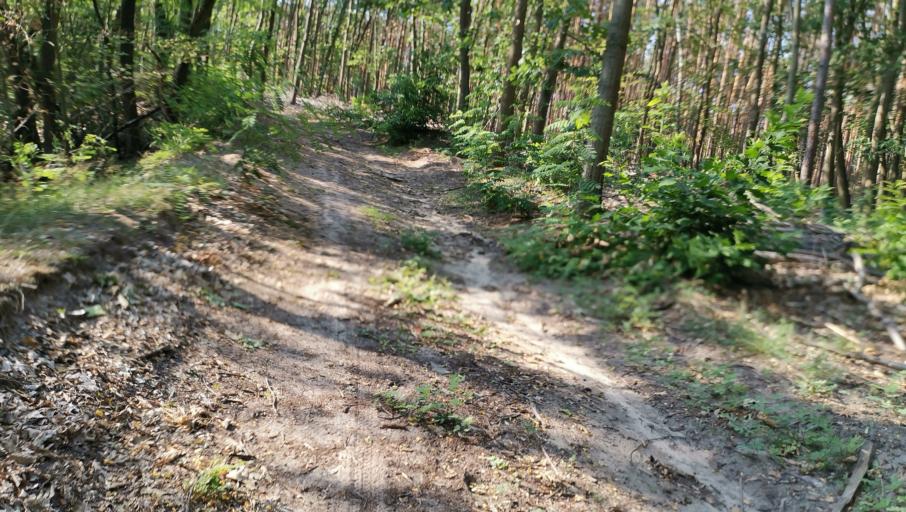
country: DE
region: Brandenburg
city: Werder
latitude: 52.3826
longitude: 12.9895
